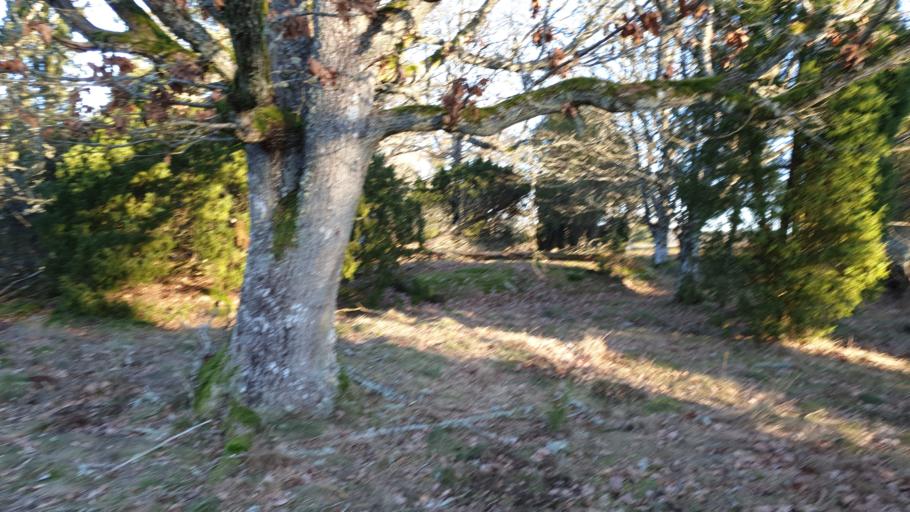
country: SE
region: Blekinge
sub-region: Ronneby Kommun
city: Brakne-Hoby
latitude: 56.2327
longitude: 15.1822
